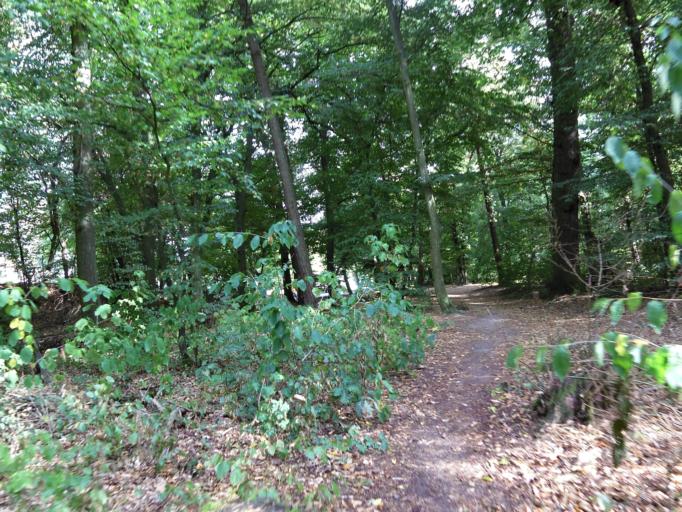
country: DE
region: Bavaria
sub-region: Regierungsbezirk Unterfranken
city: Hochberg
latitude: 49.7855
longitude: 9.8702
